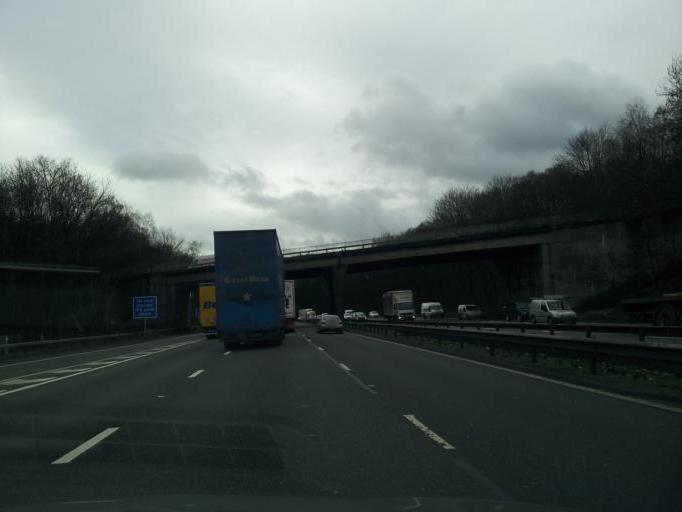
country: GB
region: England
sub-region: Staffordshire
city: Newcastle under Lyme
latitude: 52.9744
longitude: -2.2263
